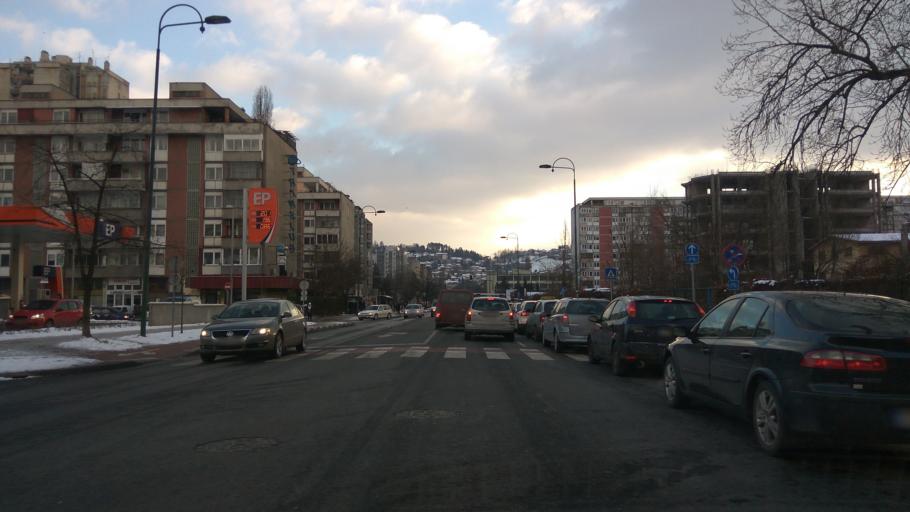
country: BA
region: Federation of Bosnia and Herzegovina
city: Kobilja Glava
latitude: 43.8565
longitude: 18.3917
